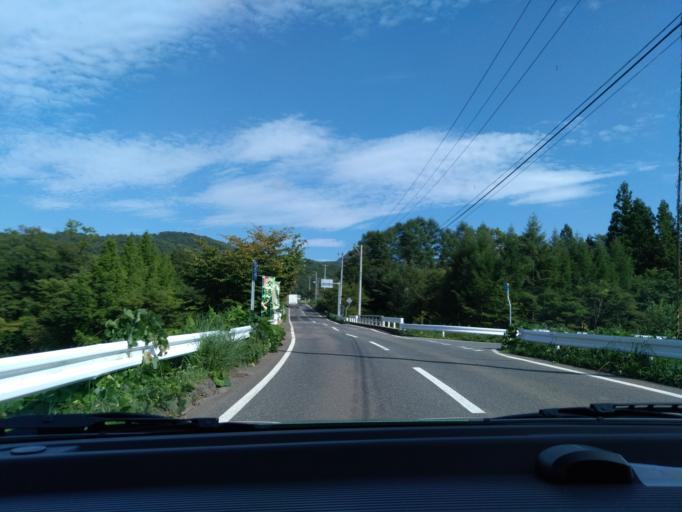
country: JP
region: Iwate
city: Shizukuishi
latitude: 39.6441
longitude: 140.9972
